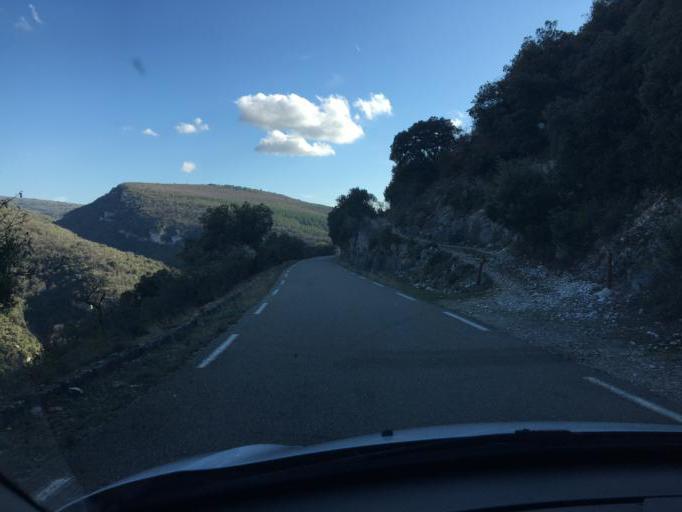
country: FR
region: Provence-Alpes-Cote d'Azur
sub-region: Departement du Vaucluse
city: Villes-sur-Auzon
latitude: 44.0525
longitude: 5.2870
